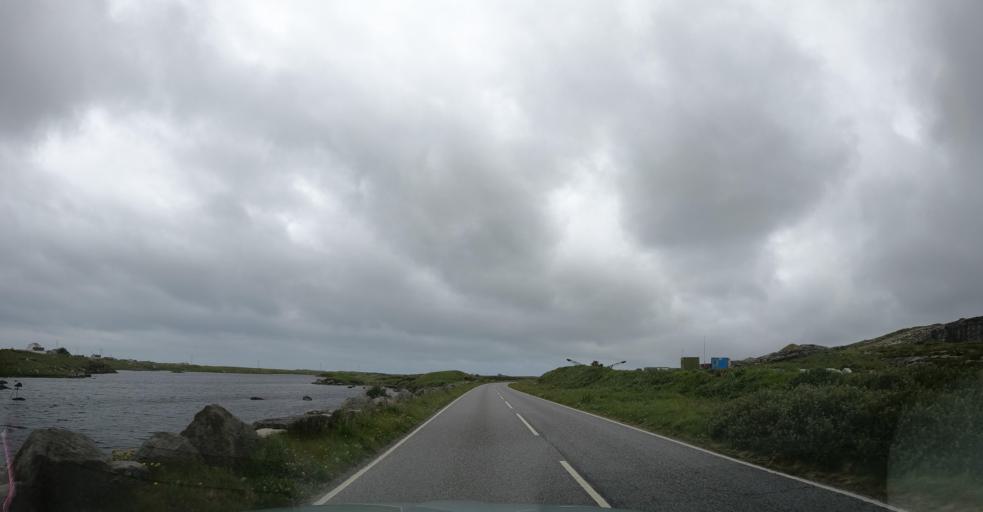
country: GB
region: Scotland
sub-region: Eilean Siar
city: Isle of South Uist
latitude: 57.1870
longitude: -7.3857
